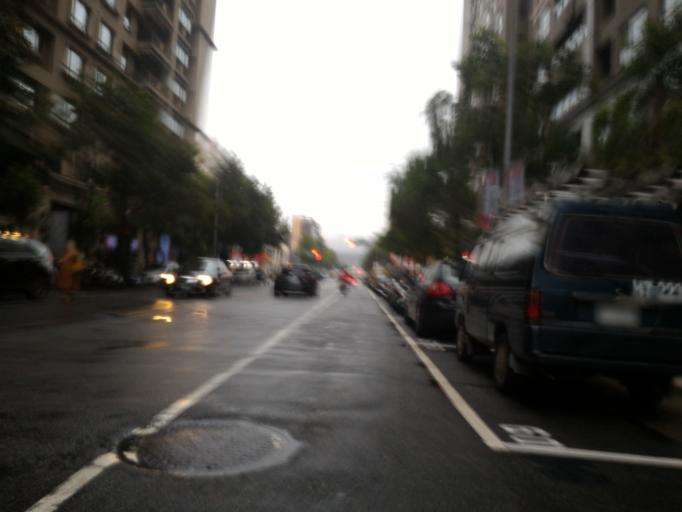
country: TW
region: Taiwan
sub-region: Taoyuan
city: Taoyuan
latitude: 24.9465
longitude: 121.3799
